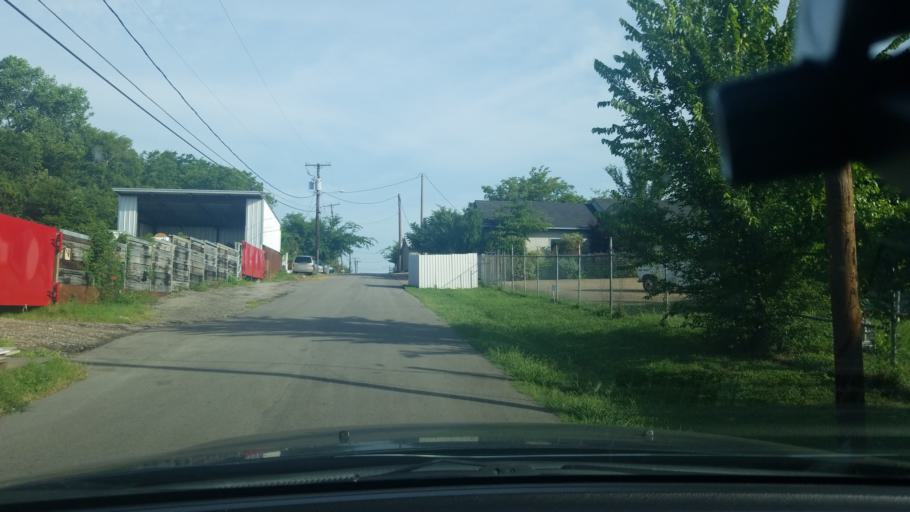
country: US
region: Texas
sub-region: Dallas County
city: Highland Park
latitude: 32.7975
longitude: -96.7150
